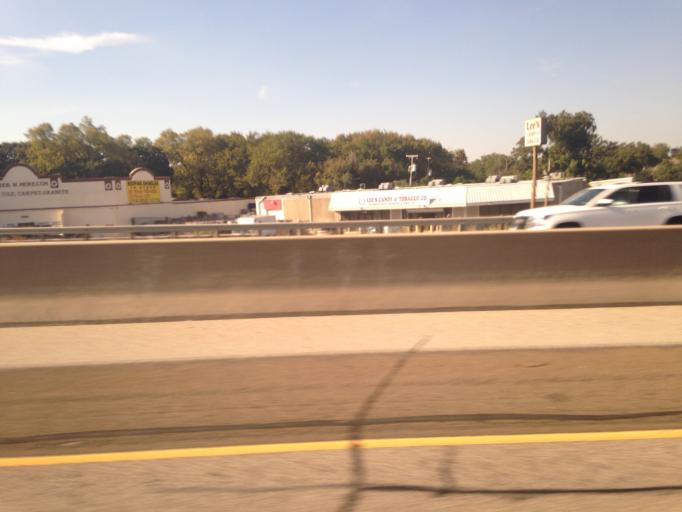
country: US
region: Texas
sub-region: Tarrant County
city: Haltom City
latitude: 32.7795
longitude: -97.2779
